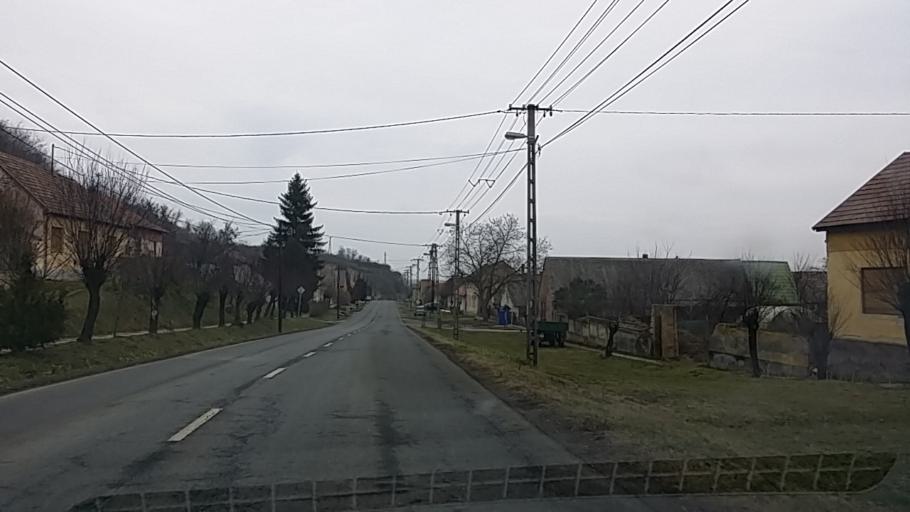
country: HU
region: Baranya
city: Dunaszekcso
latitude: 46.0778
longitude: 18.7555
